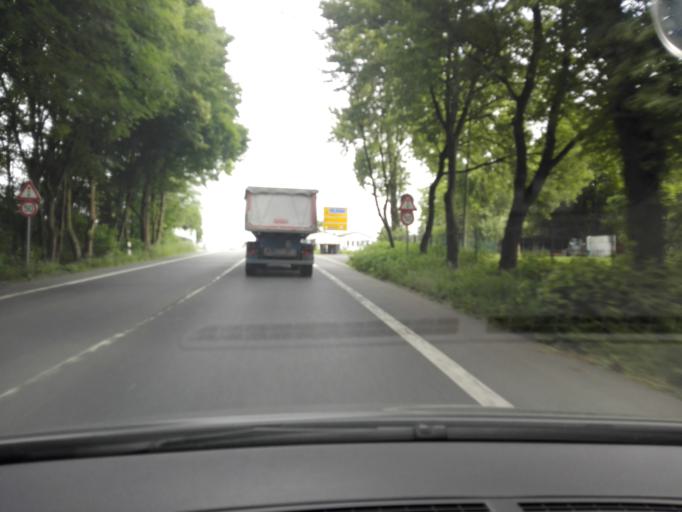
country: DE
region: North Rhine-Westphalia
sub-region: Regierungsbezirk Arnsberg
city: Unna
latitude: 51.4985
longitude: 7.7042
